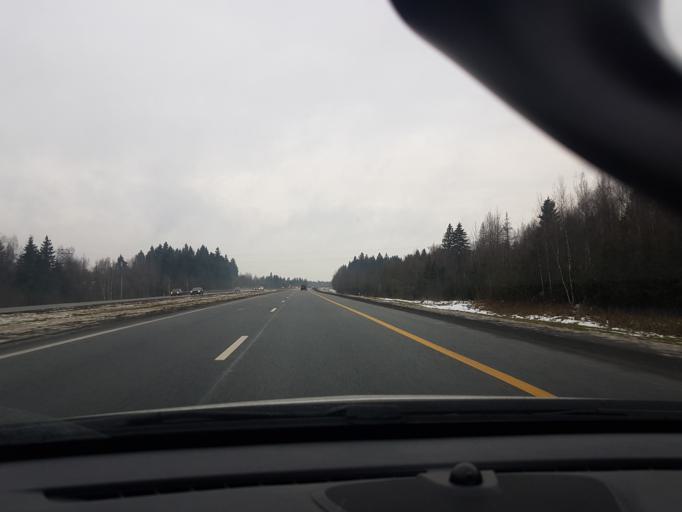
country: RU
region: Moskovskaya
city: Novopetrovskoye
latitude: 55.9814
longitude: 36.3888
